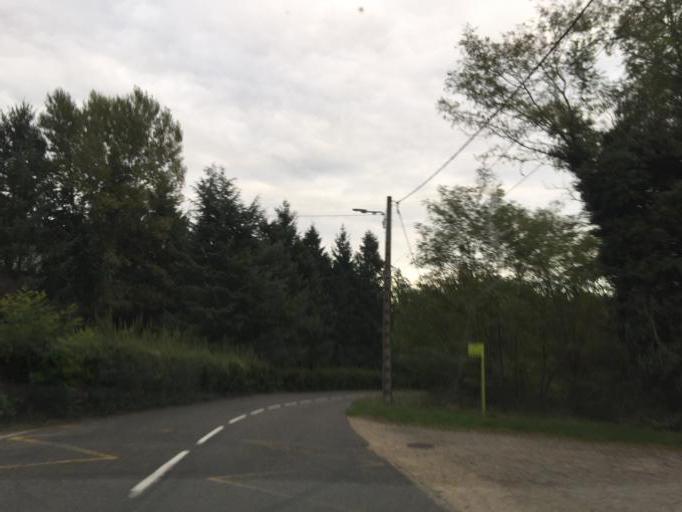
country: FR
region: Rhone-Alpes
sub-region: Departement de la Loire
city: La Grand-Croix
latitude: 45.5089
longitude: 4.5610
